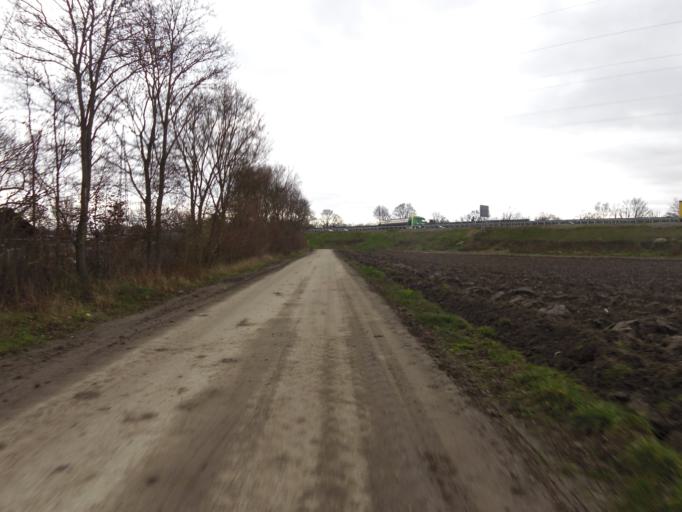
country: DE
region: Rheinland-Pfalz
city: Frankenthal
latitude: 49.5560
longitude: 8.3758
